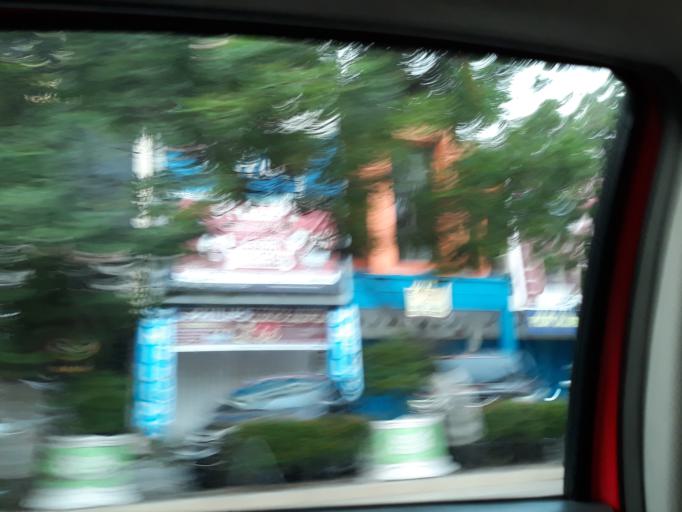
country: ID
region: East Kalimantan
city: Balikpapan
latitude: -1.2772
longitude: 116.8358
